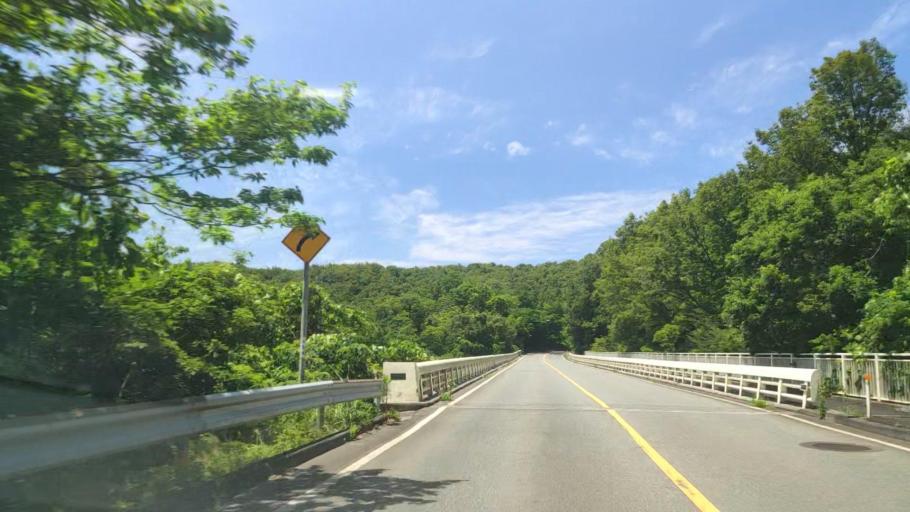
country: JP
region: Tottori
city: Tottori
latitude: 35.5283
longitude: 134.2298
